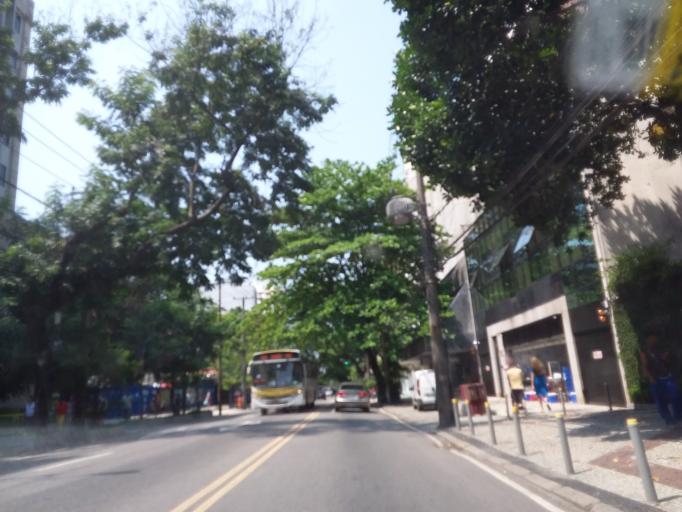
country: BR
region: Rio de Janeiro
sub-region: Rio De Janeiro
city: Rio de Janeiro
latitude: -22.9770
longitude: -43.2301
